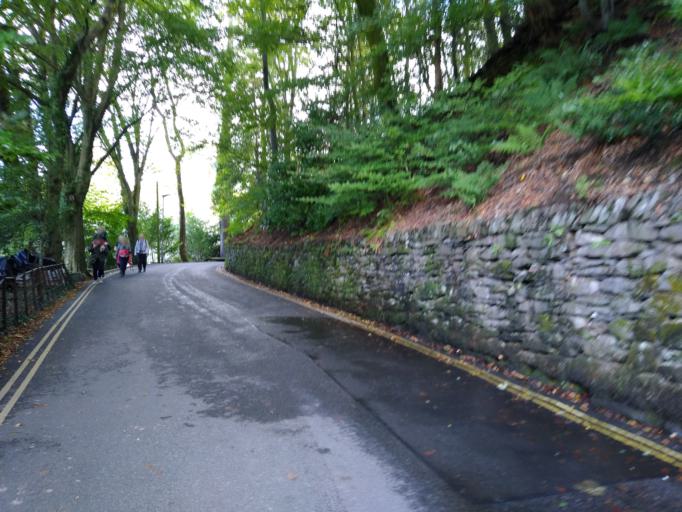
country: GB
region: England
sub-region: Cumbria
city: Ambleside
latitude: 54.4321
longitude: -2.9611
